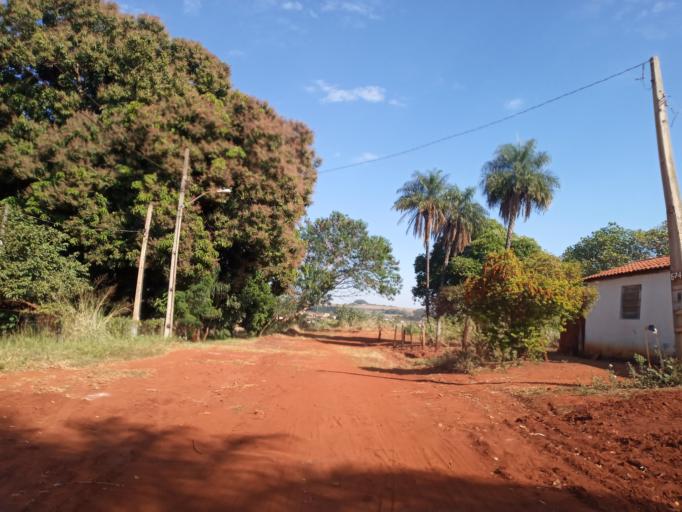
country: BR
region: Minas Gerais
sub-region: Ituiutaba
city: Ituiutaba
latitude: -18.9967
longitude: -49.4649
